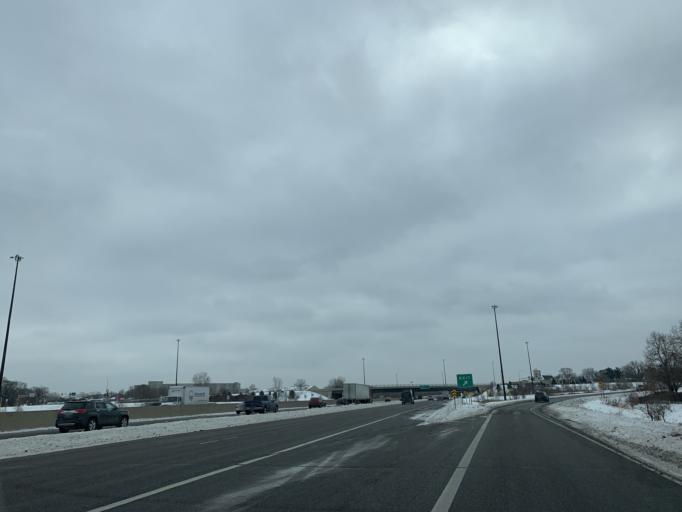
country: US
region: Minnesota
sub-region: Anoka County
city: Coon Rapids
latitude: 45.1547
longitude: -93.2775
